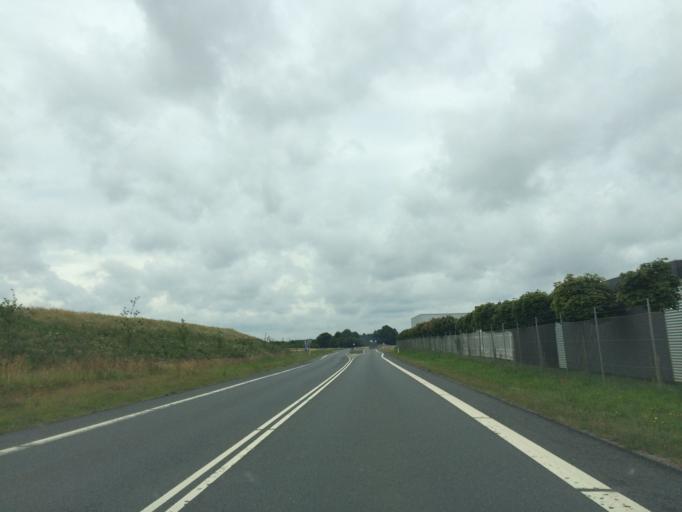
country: DK
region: Central Jutland
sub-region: Silkeborg Kommune
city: Svejbaek
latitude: 56.2212
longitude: 9.6263
